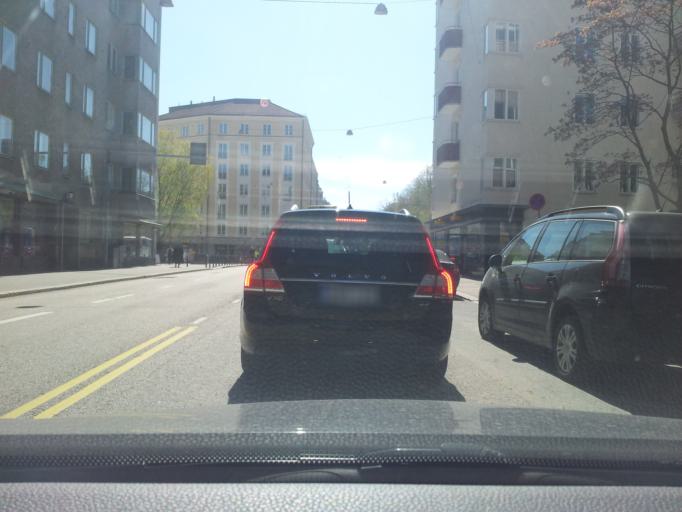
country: FI
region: Uusimaa
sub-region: Helsinki
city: Helsinki
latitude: 60.1843
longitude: 24.9175
